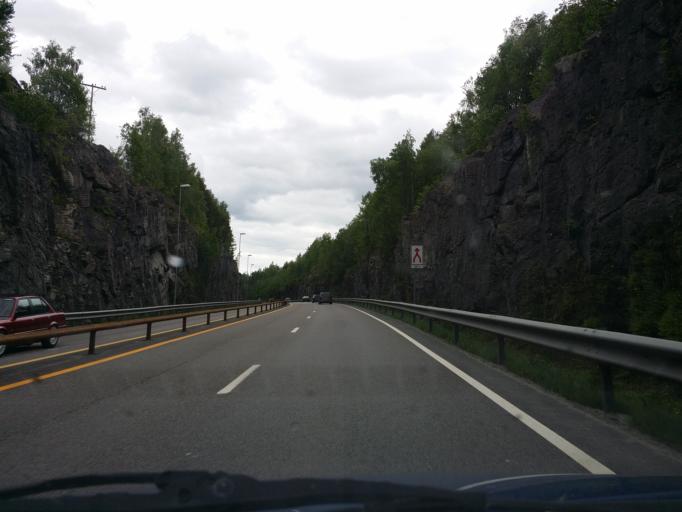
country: NO
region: Hedmark
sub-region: Ringsaker
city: Brumunddal
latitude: 60.8549
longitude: 10.9844
